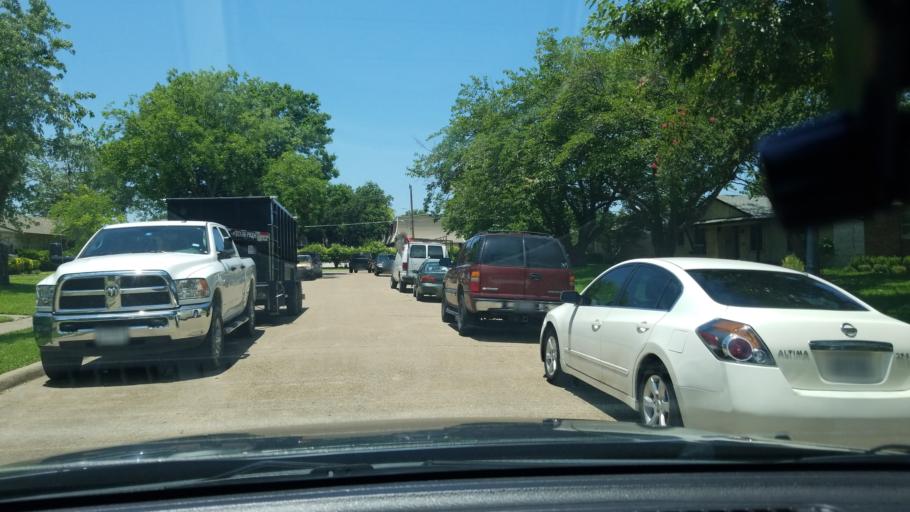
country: US
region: Texas
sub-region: Dallas County
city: Mesquite
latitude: 32.7960
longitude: -96.6496
